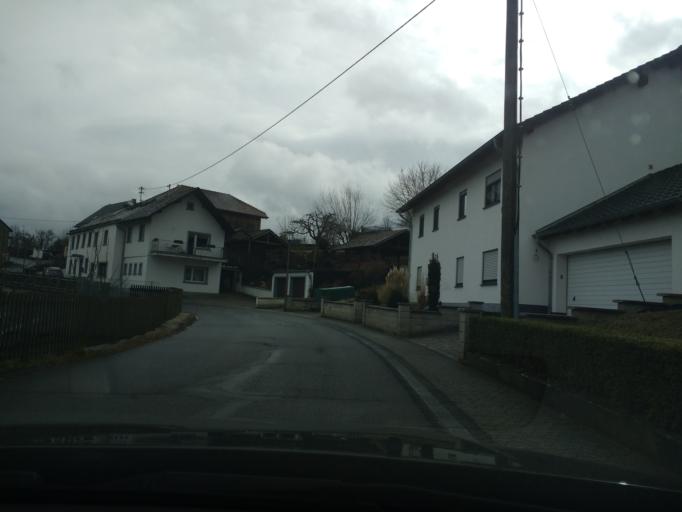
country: DE
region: Rheinland-Pfalz
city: Ollmuth
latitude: 49.6705
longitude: 6.7144
